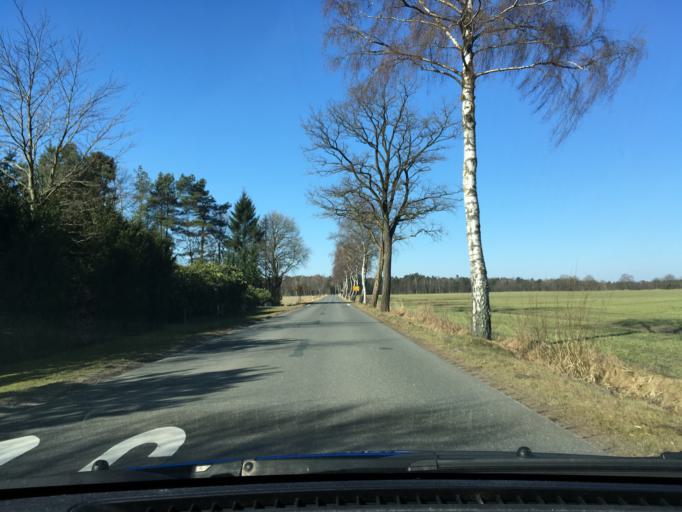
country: DE
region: Lower Saxony
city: Schneverdingen
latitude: 53.0822
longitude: 9.8463
